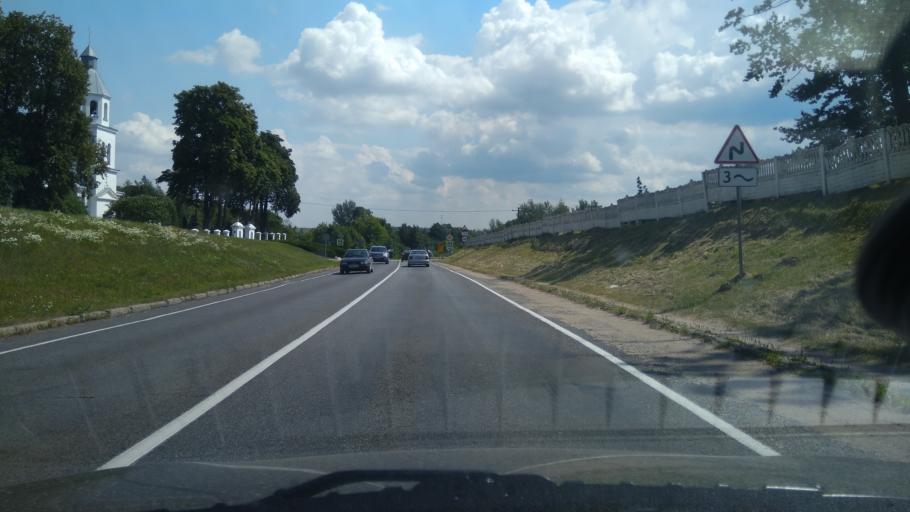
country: BY
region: Brest
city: Lyakhavichy
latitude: 53.1137
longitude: 26.1632
